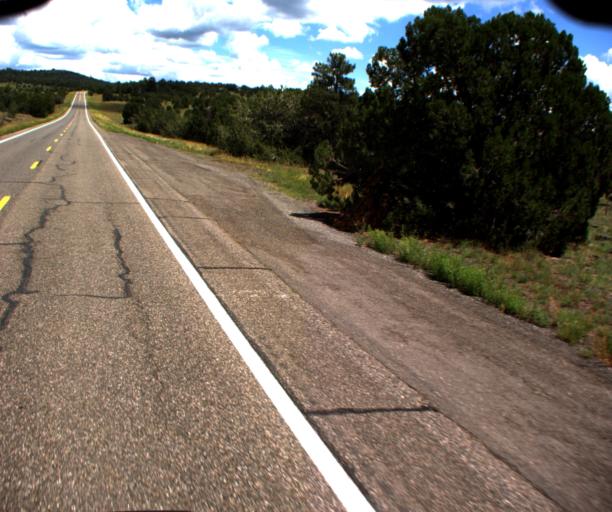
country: US
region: Arizona
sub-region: Gila County
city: Pine
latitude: 34.5069
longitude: -111.5666
